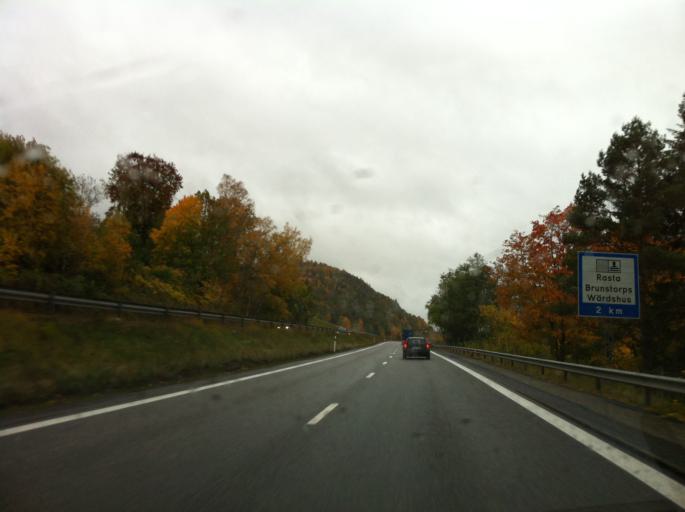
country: SE
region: Joenkoeping
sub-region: Jonkopings Kommun
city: Kaxholmen
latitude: 57.8429
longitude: 14.2680
